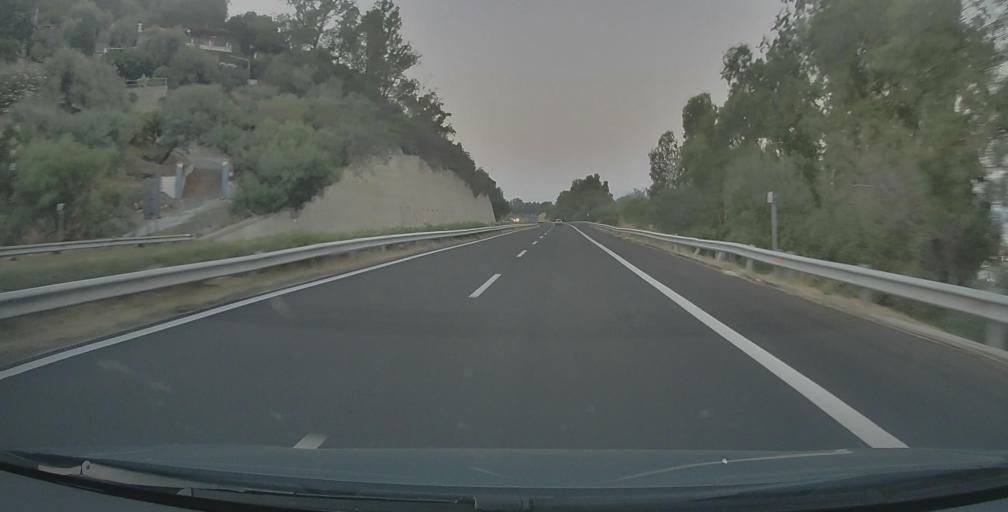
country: IT
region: Sicily
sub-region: Messina
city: Sant'Alessio Siculo
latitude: 37.9236
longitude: 15.3456
